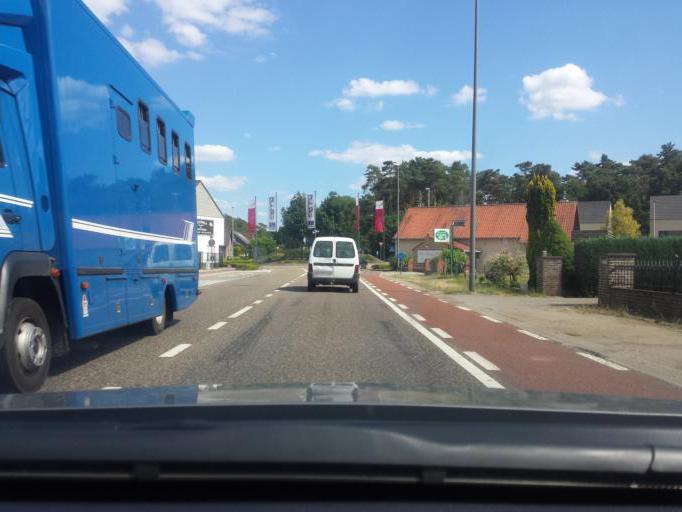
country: BE
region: Flanders
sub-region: Provincie Limburg
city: Heusden
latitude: 51.0309
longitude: 5.2568
